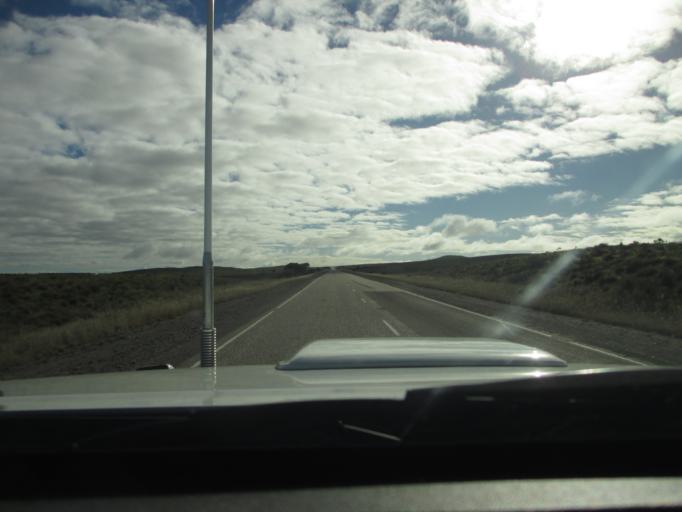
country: AU
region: South Australia
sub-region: Peterborough
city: Peterborough
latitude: -32.5811
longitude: 138.5614
